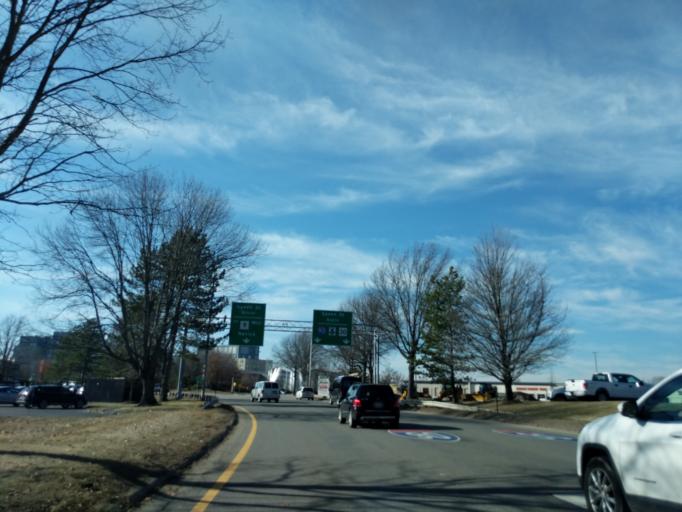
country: US
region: Massachusetts
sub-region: Middlesex County
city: Cochituate
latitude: 42.3021
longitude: -71.3785
